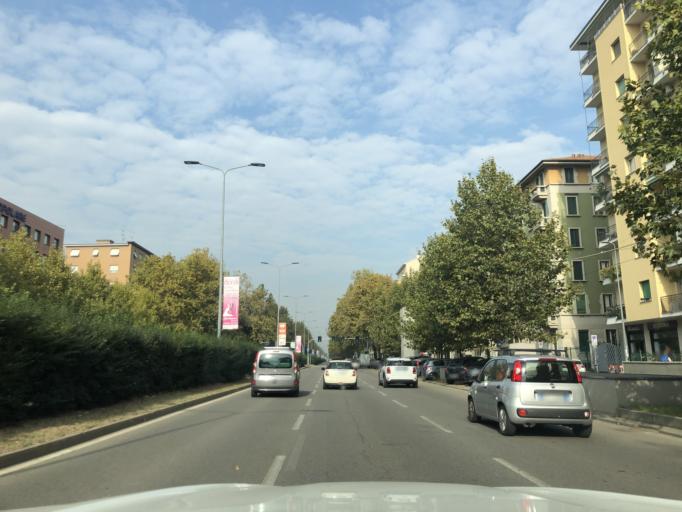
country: IT
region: Lombardy
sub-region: Citta metropolitana di Milano
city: Bresso
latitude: 45.5070
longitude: 9.2011
